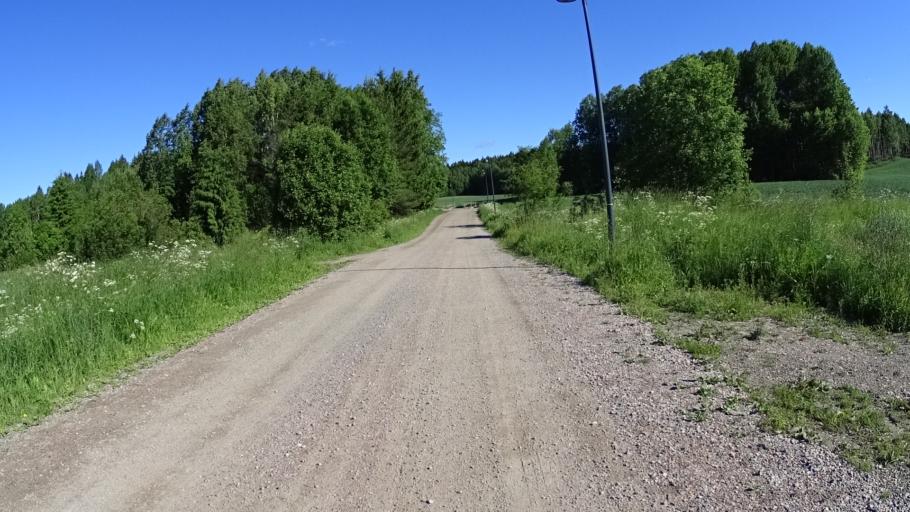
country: FI
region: Uusimaa
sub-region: Helsinki
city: Kilo
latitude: 60.2918
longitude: 24.8155
